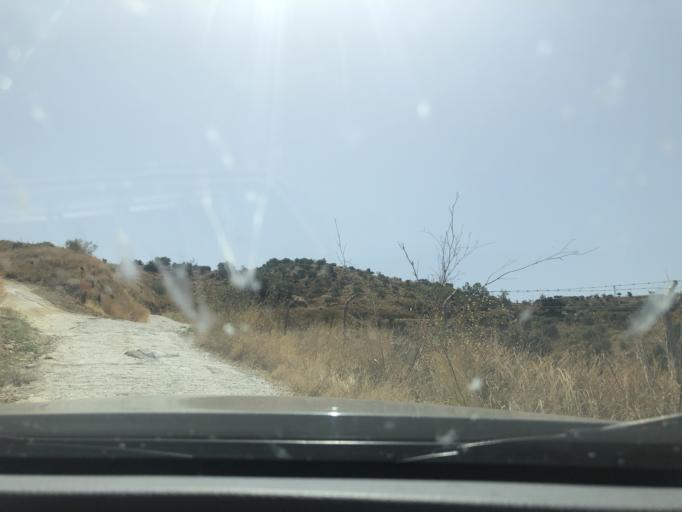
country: ES
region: Andalusia
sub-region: Provincia de Malaga
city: Cartama
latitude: 36.7090
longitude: -4.6260
